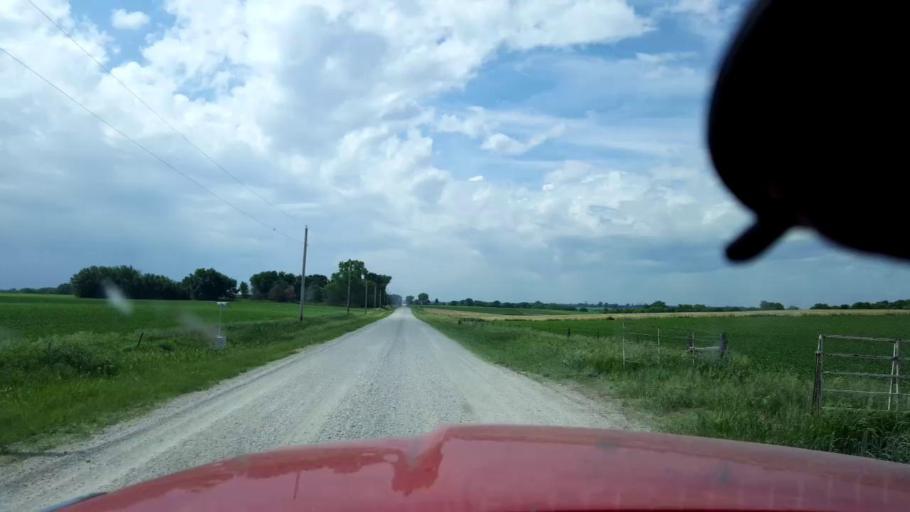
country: US
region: Iowa
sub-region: Cherokee County
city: Cherokee
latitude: 42.8213
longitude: -95.5346
